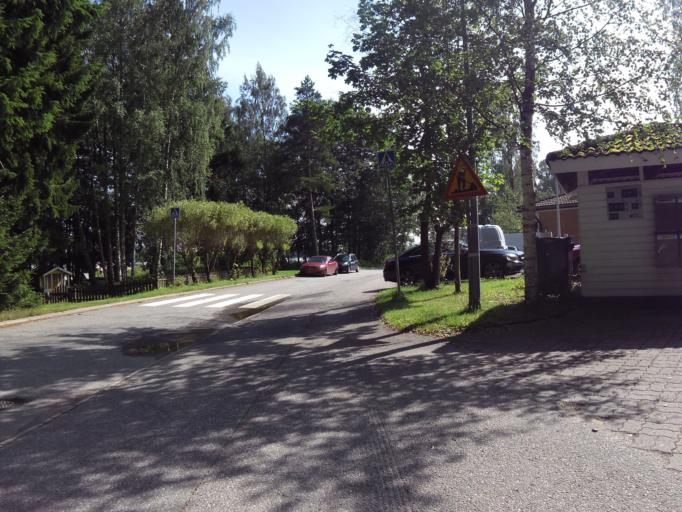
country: FI
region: Uusimaa
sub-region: Helsinki
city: Koukkuniemi
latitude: 60.1461
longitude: 24.7118
